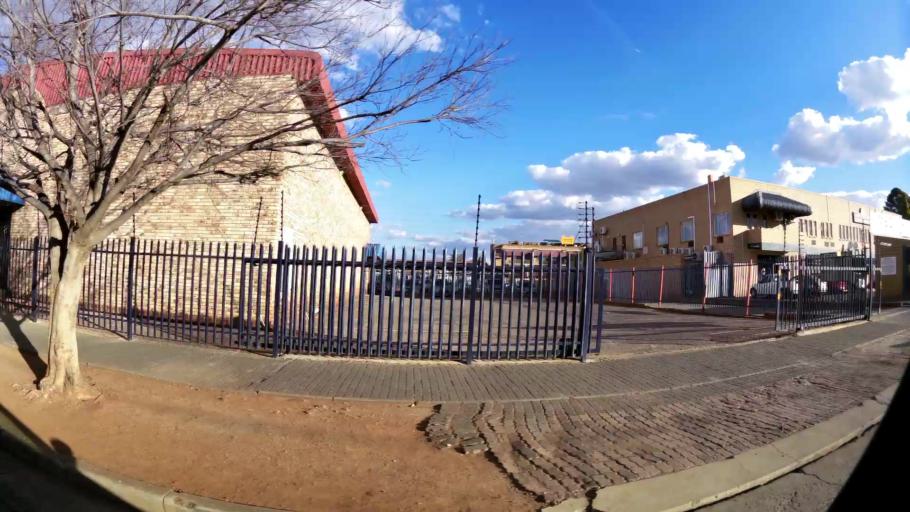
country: ZA
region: North-West
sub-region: Dr Kenneth Kaunda District Municipality
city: Potchefstroom
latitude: -26.7107
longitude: 27.0941
